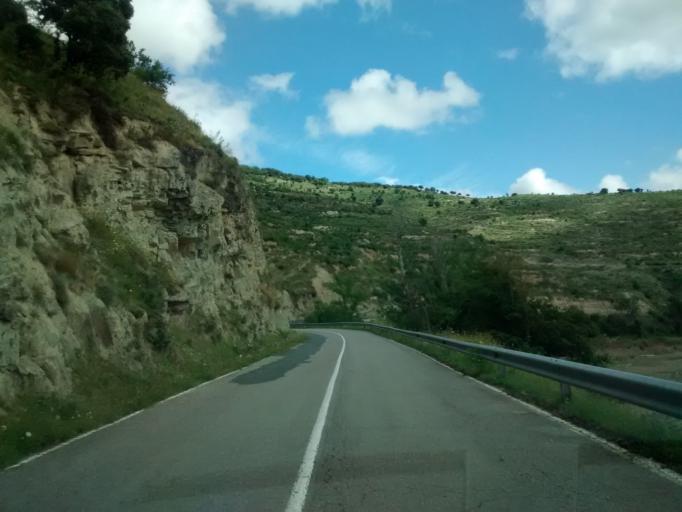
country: ES
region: La Rioja
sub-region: Provincia de La Rioja
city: Terroba
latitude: 42.2541
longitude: -2.4546
